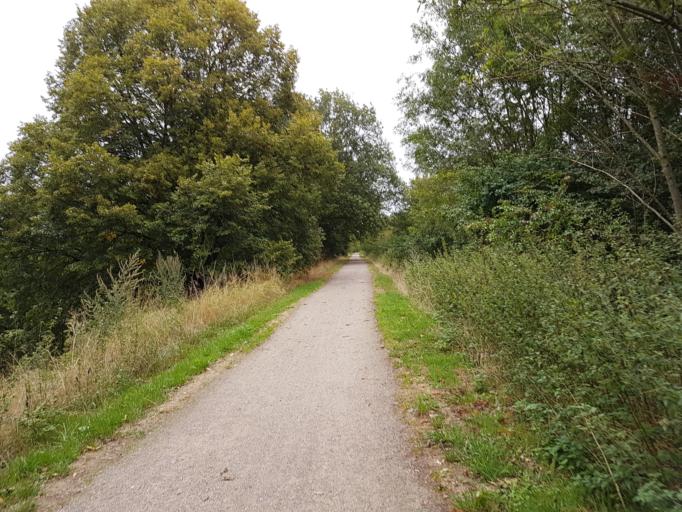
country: DE
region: North Rhine-Westphalia
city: Olfen
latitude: 51.7122
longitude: 7.3931
